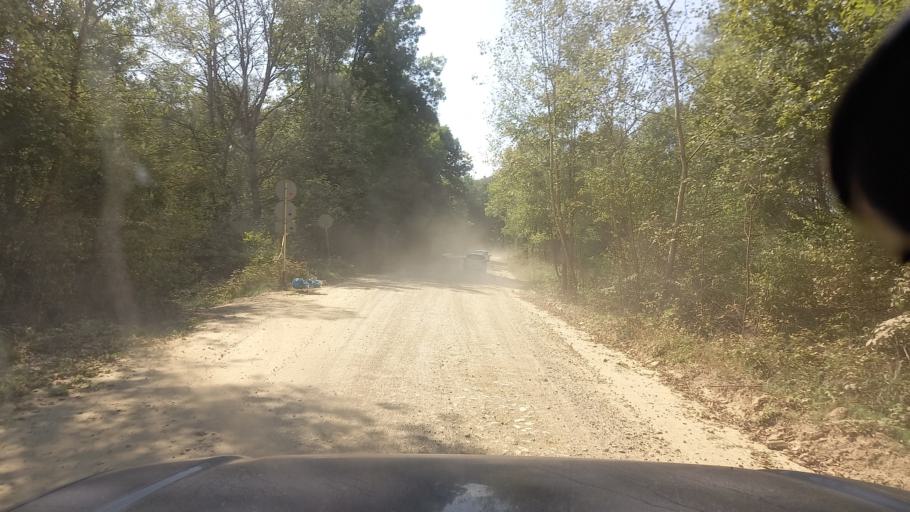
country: RU
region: Krasnodarskiy
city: Azovskaya
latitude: 44.6956
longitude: 38.6443
